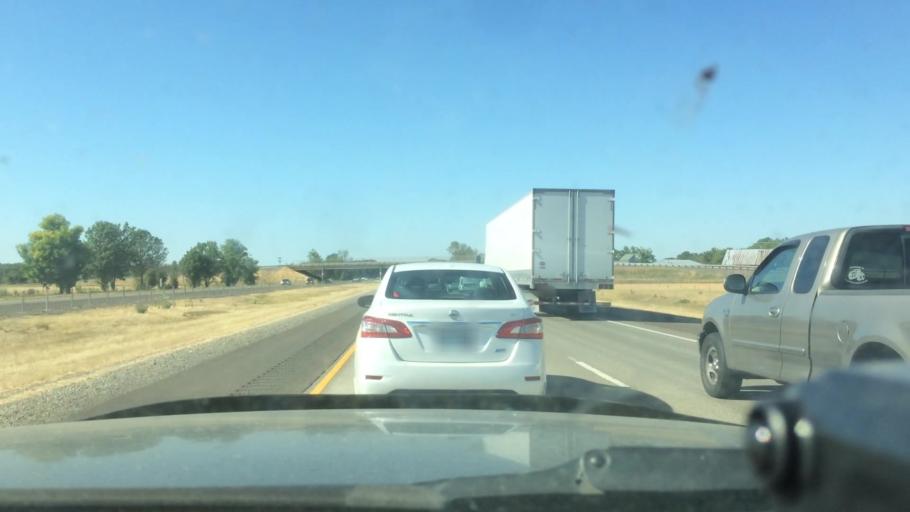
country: US
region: Oregon
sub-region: Linn County
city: Tangent
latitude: 44.5823
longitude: -123.0631
